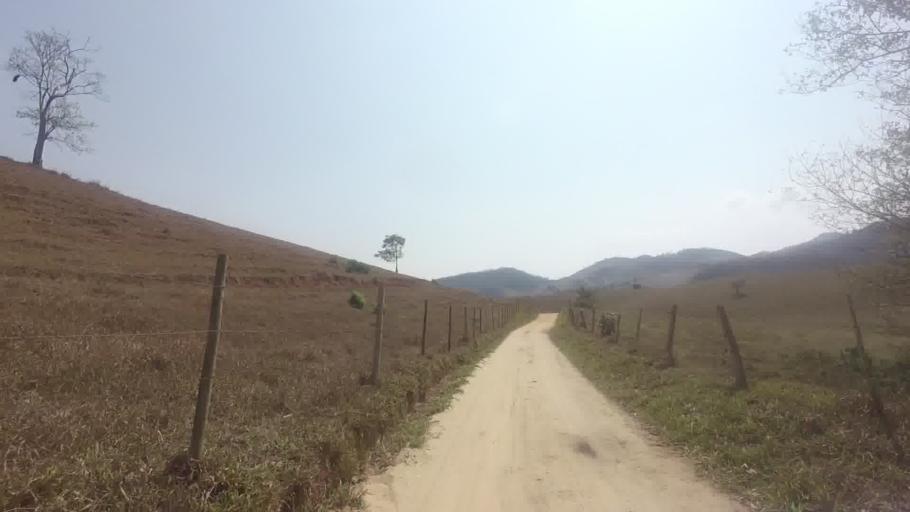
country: BR
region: Espirito Santo
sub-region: Sao Jose Do Calcado
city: Sao Jose do Calcado
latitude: -21.0380
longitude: -41.5243
